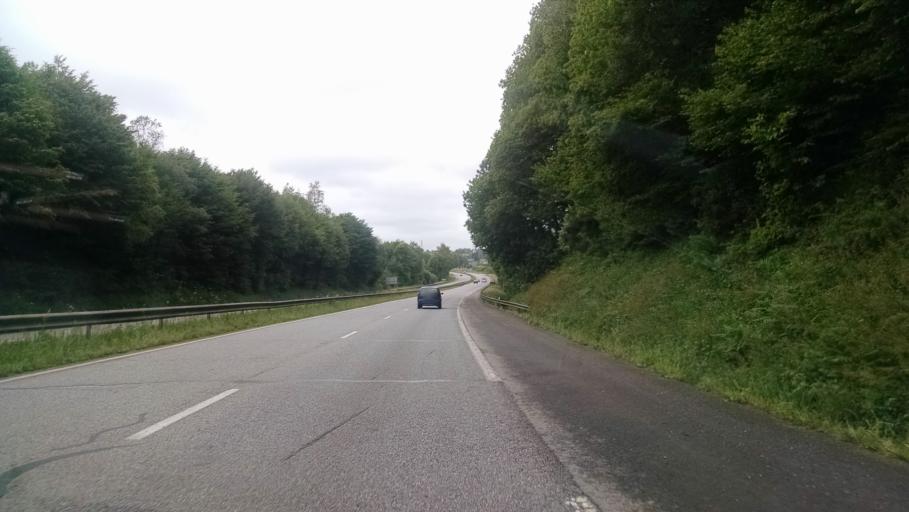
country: FR
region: Brittany
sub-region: Departement du Finistere
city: Quimper
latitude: 48.0091
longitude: -4.0664
